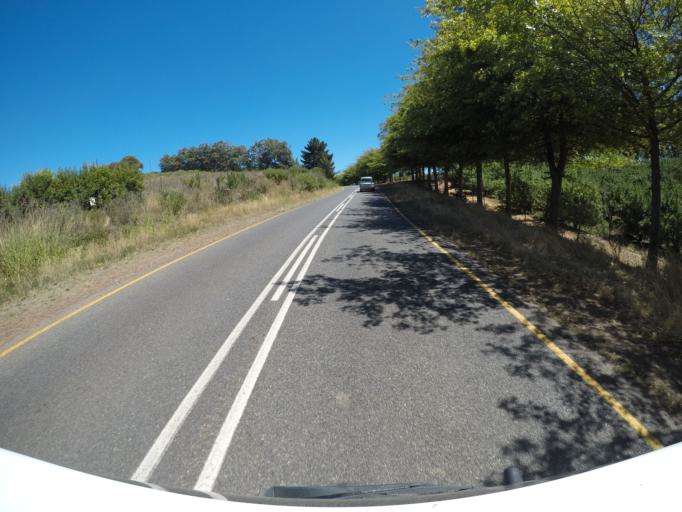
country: ZA
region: Western Cape
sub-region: Overberg District Municipality
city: Grabouw
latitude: -34.2102
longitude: 19.0437
